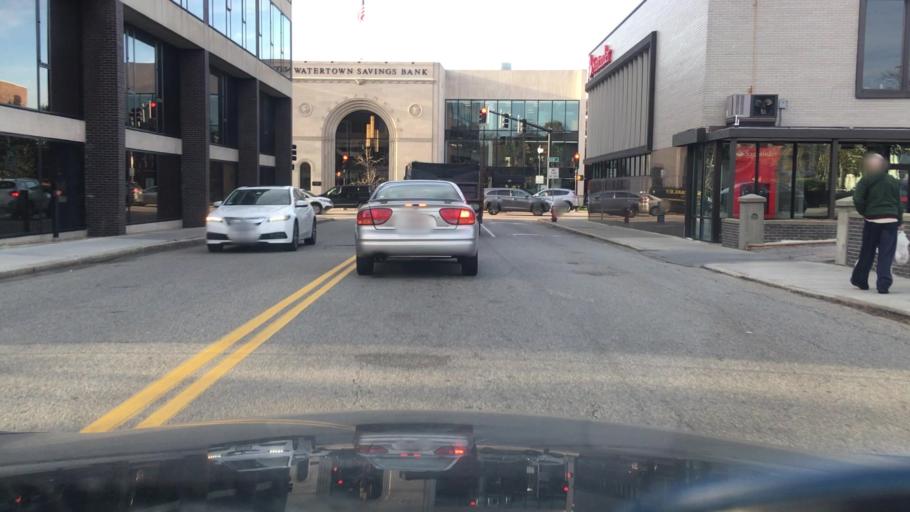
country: US
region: Massachusetts
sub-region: Middlesex County
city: Watertown
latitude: 42.3669
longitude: -71.1856
